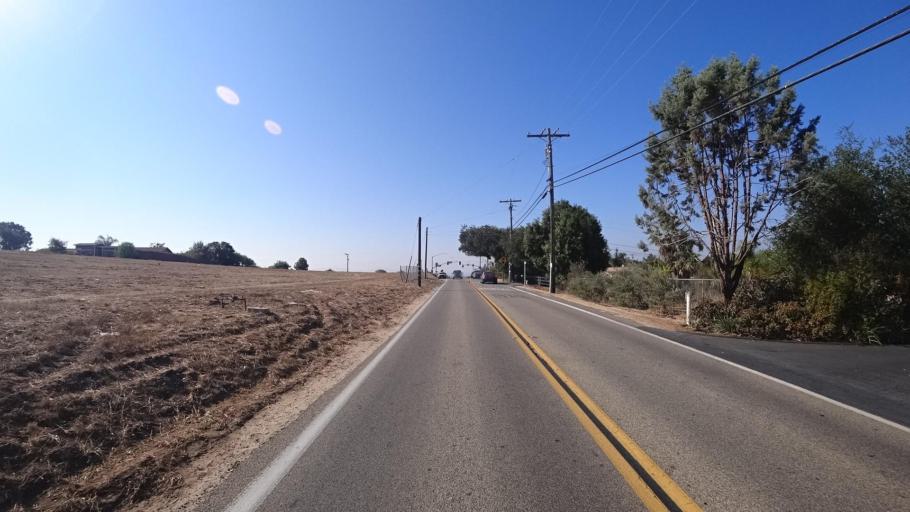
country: US
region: California
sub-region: San Diego County
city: Fallbrook
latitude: 33.3779
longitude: -117.2278
